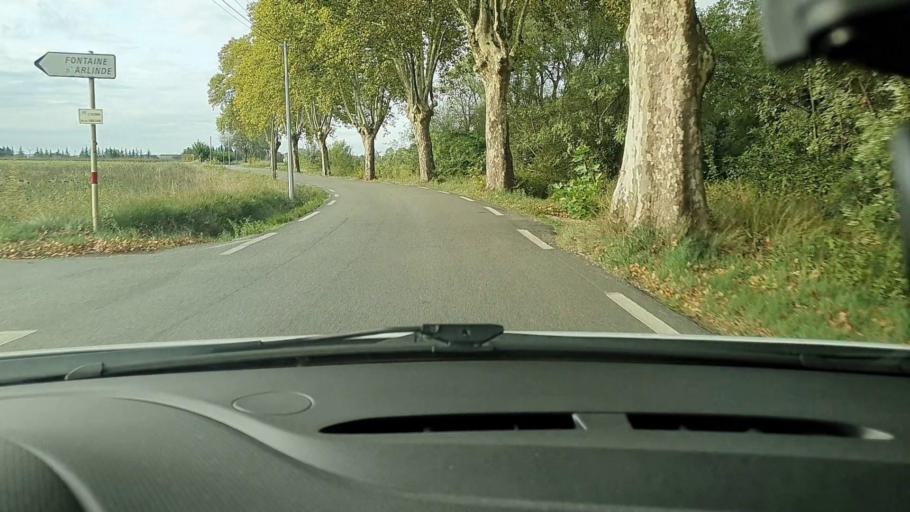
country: FR
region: Languedoc-Roussillon
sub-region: Departement du Gard
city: Les Mages
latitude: 44.1910
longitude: 4.2380
